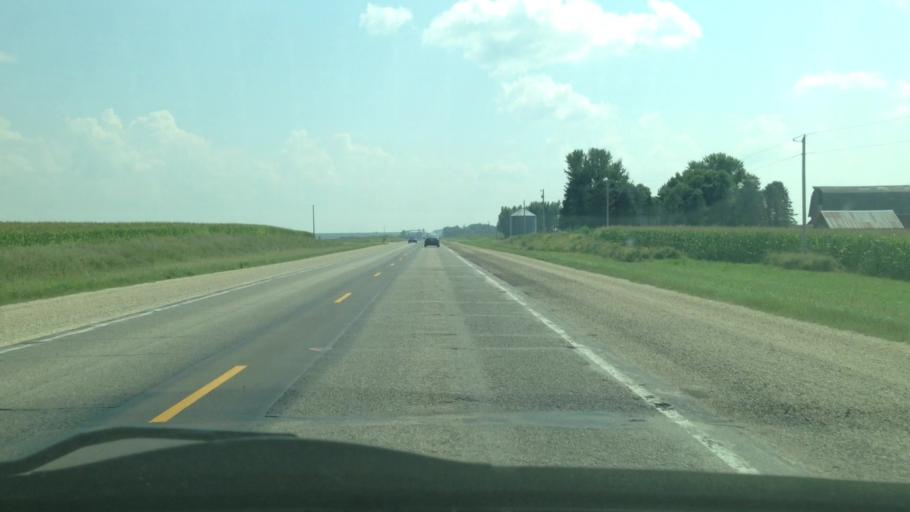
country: US
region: Iowa
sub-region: Howard County
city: Cresco
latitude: 43.3565
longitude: -92.2985
